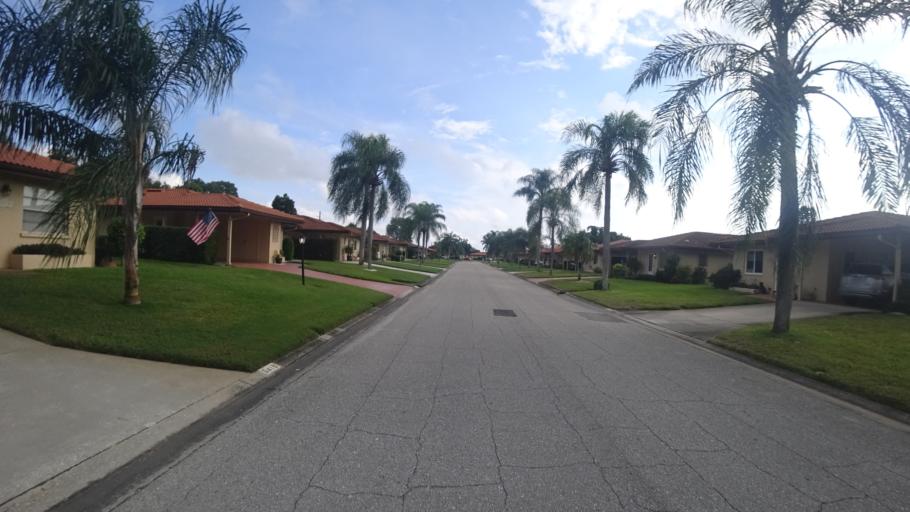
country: US
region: Florida
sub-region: Manatee County
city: Bayshore Gardens
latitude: 27.4265
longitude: -82.5920
